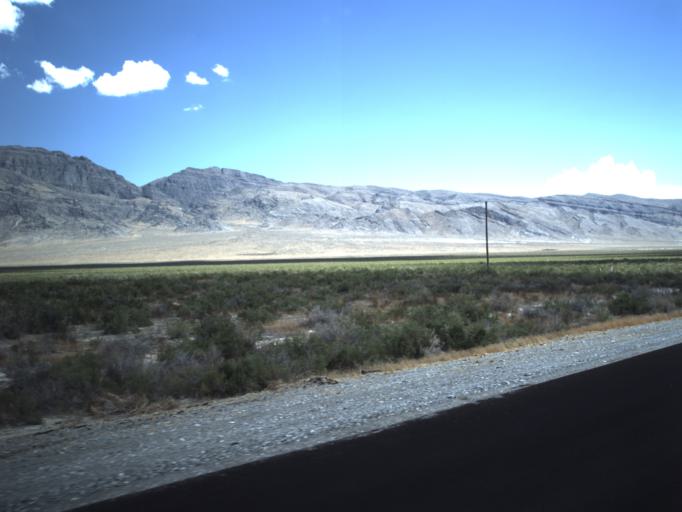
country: US
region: Utah
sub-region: Beaver County
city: Milford
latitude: 39.0798
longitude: -113.4861
